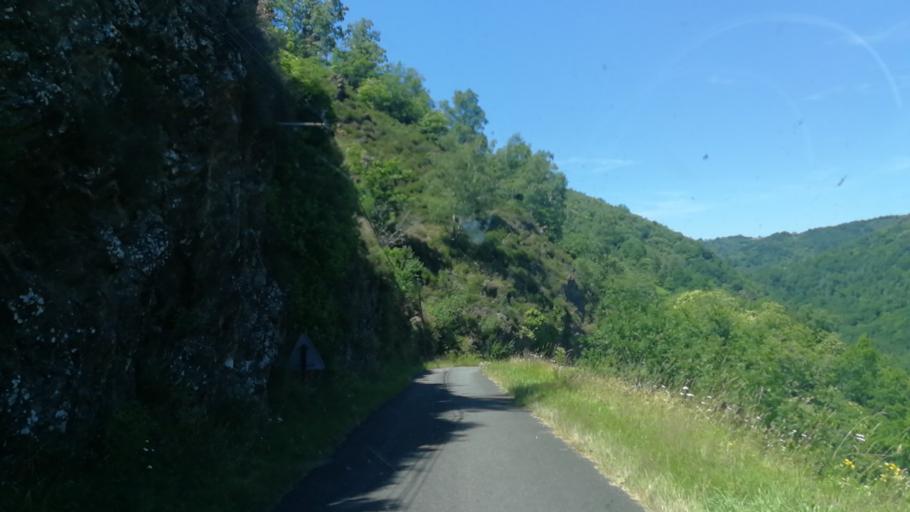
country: FR
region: Midi-Pyrenees
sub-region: Departement de l'Aveyron
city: Firmi
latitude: 44.5956
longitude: 2.3915
